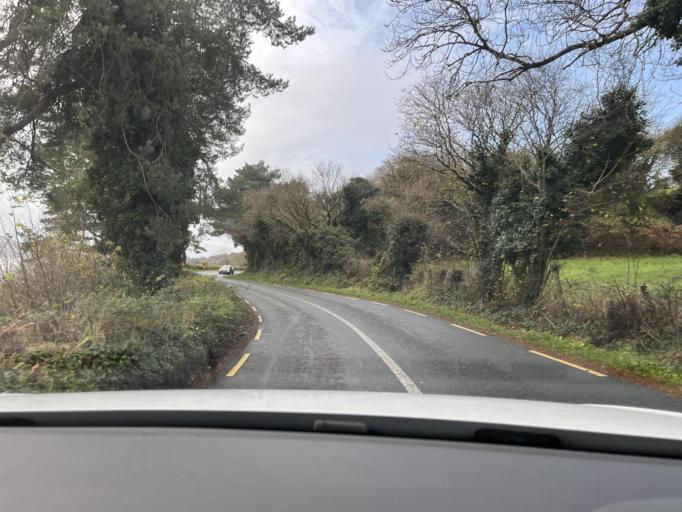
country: IE
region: Connaught
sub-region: Sligo
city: Sligo
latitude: 54.2658
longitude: -8.3373
